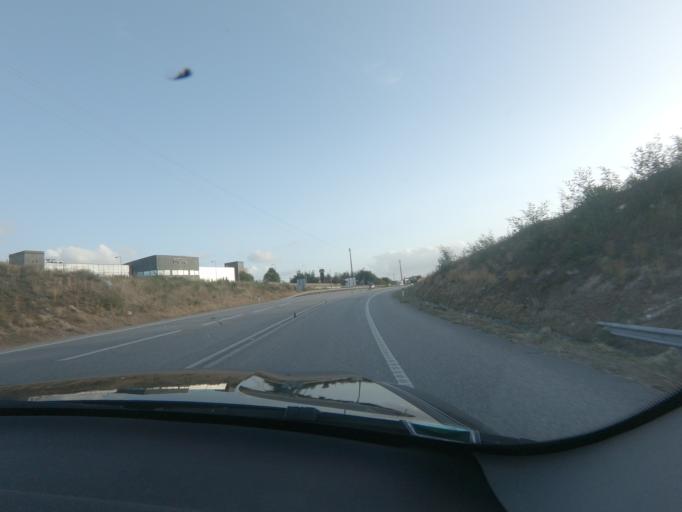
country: PT
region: Viseu
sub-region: Santa Comba Dao
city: Santa Comba Dao
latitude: 40.3612
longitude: -8.1350
